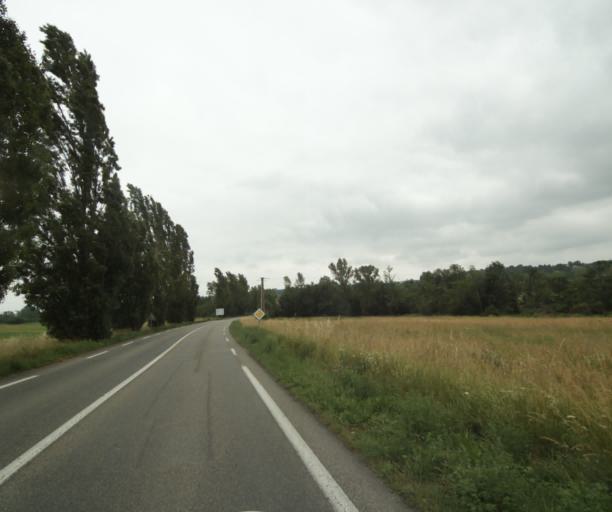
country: FR
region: Midi-Pyrenees
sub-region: Departement du Tarn-et-Garonne
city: Saint-Nauphary
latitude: 43.9893
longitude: 1.3927
